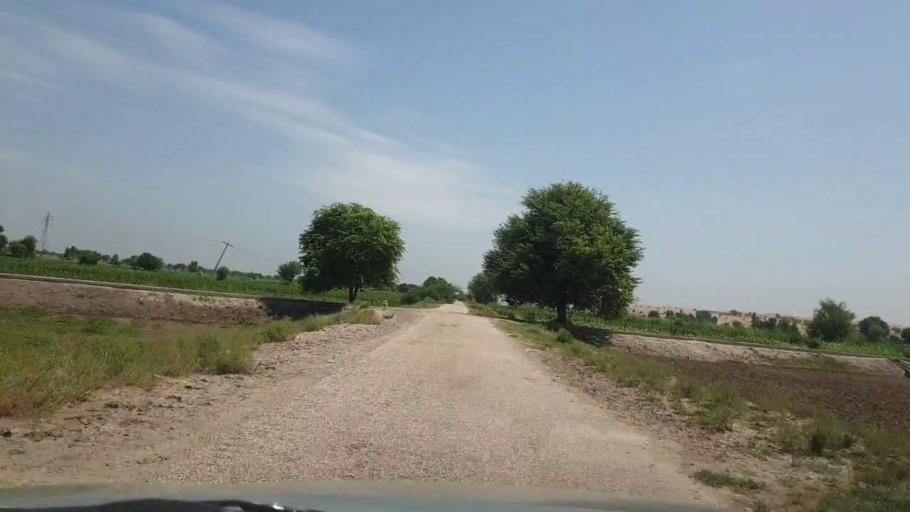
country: PK
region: Sindh
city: Bozdar
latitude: 27.0941
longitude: 68.9709
